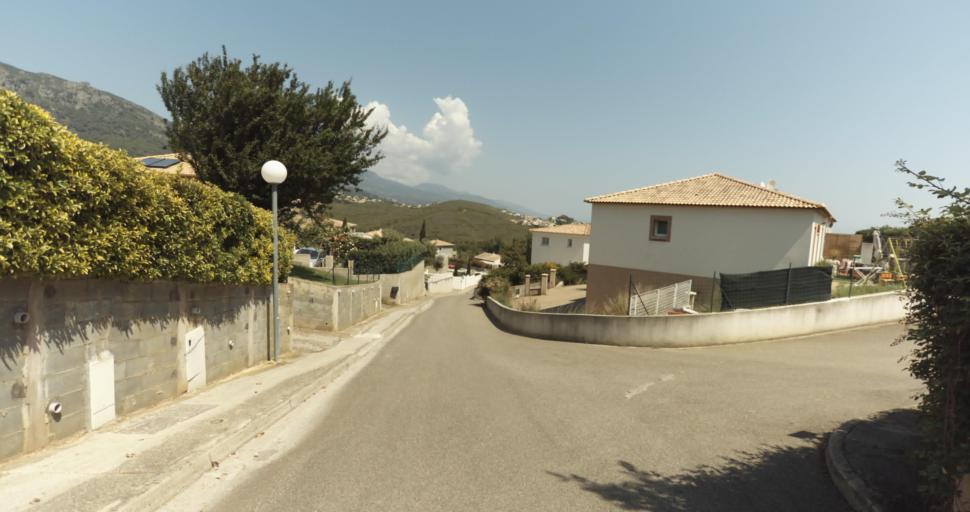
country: FR
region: Corsica
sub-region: Departement de la Haute-Corse
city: Biguglia
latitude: 42.6059
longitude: 9.4279
